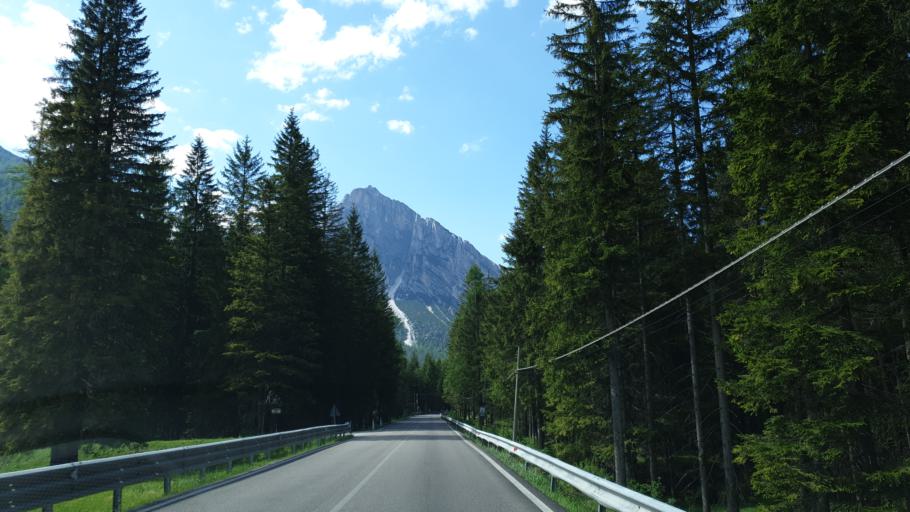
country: IT
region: Veneto
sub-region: Provincia di Belluno
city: Cortina d'Ampezzo
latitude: 46.5673
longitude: 12.1208
